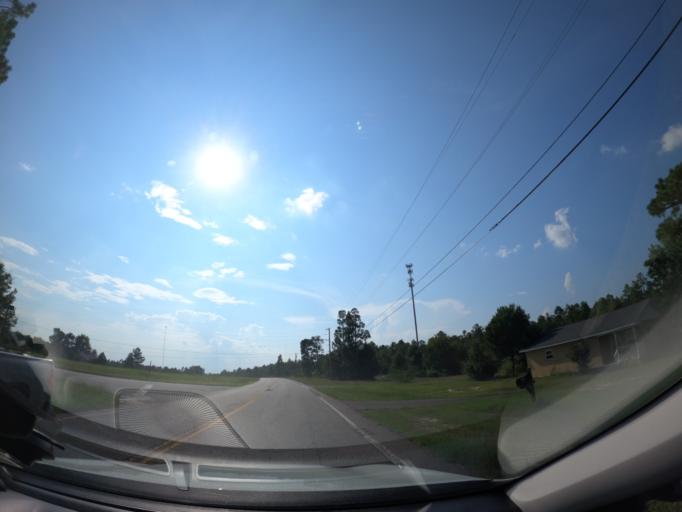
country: US
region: South Carolina
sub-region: Aiken County
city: Jackson
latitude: 33.4112
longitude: -81.8016
